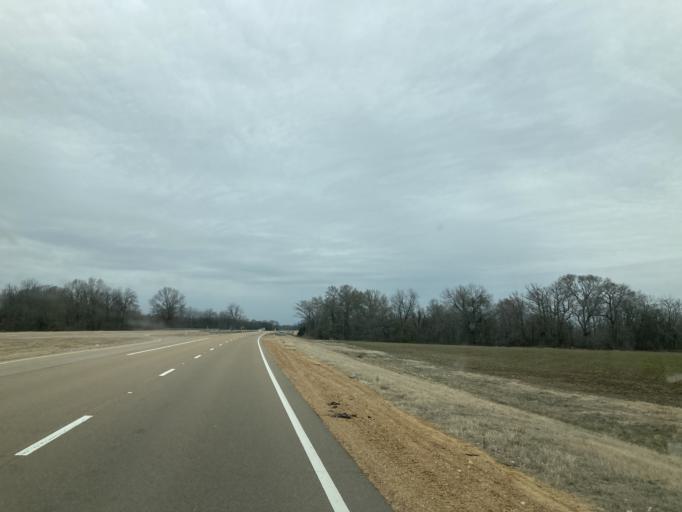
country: US
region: Mississippi
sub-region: Yazoo County
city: Yazoo City
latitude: 32.9965
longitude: -90.4695
